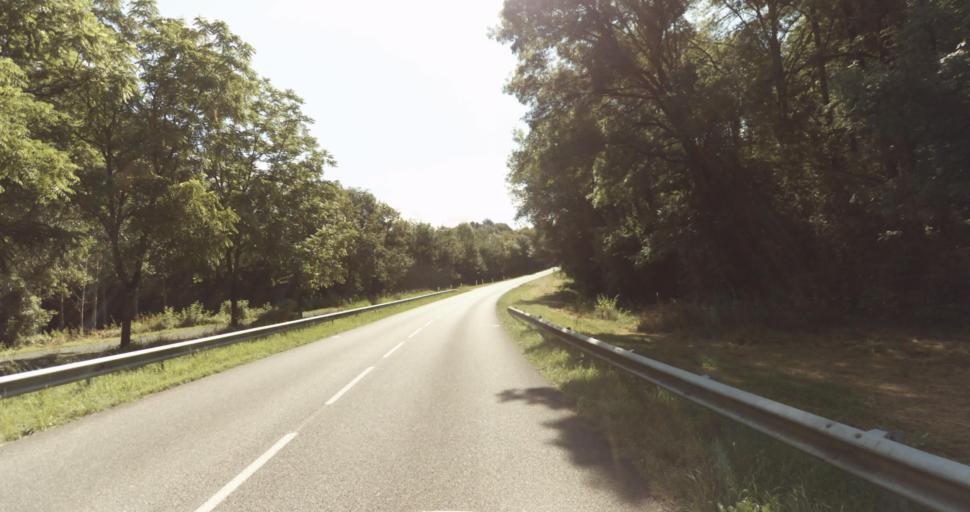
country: FR
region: Aquitaine
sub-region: Departement de la Gironde
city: Bazas
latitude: 44.4431
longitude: -0.1669
